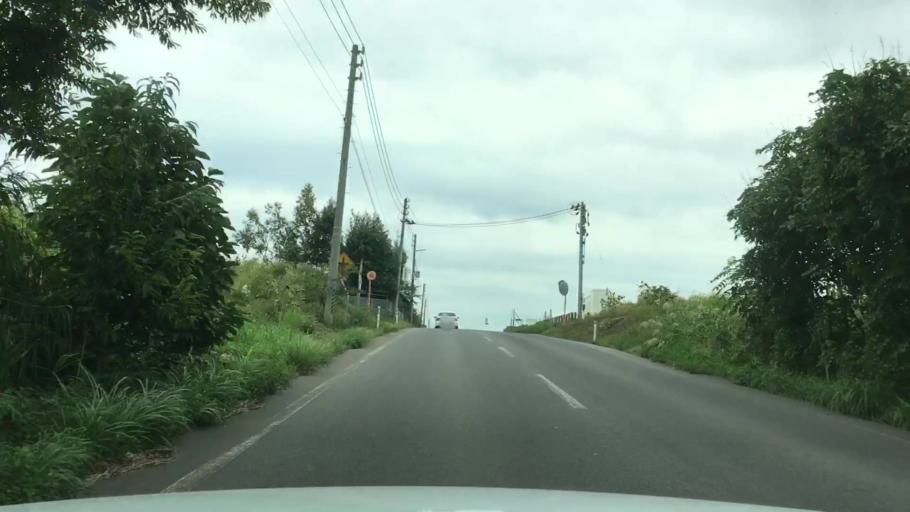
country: JP
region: Aomori
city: Hirosaki
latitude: 40.6531
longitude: 140.4215
